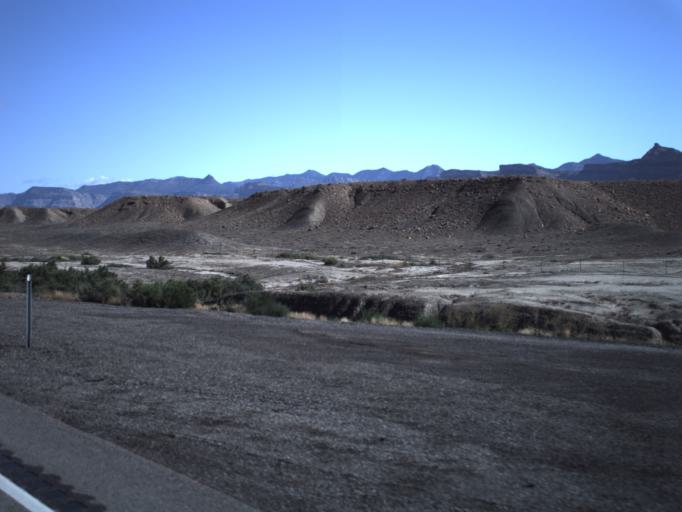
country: US
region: Utah
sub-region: Carbon County
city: East Carbon City
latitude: 39.2943
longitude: -110.3540
